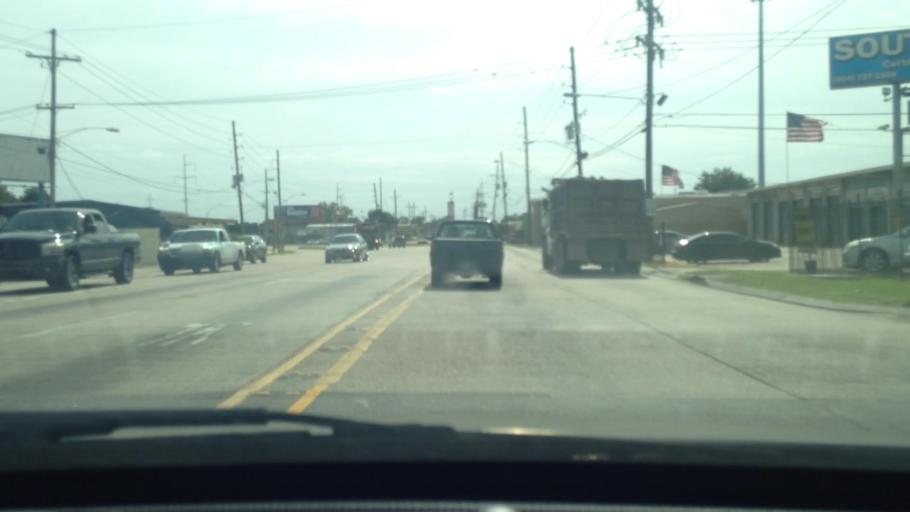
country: US
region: Louisiana
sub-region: Jefferson Parish
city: River Ridge
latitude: 29.9775
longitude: -90.2108
